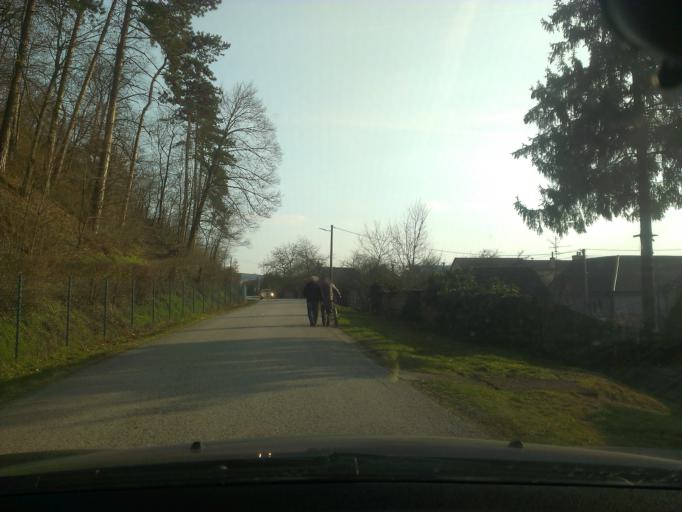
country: SK
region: Trnavsky
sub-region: Okres Trnava
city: Piestany
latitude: 48.6603
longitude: 17.8794
